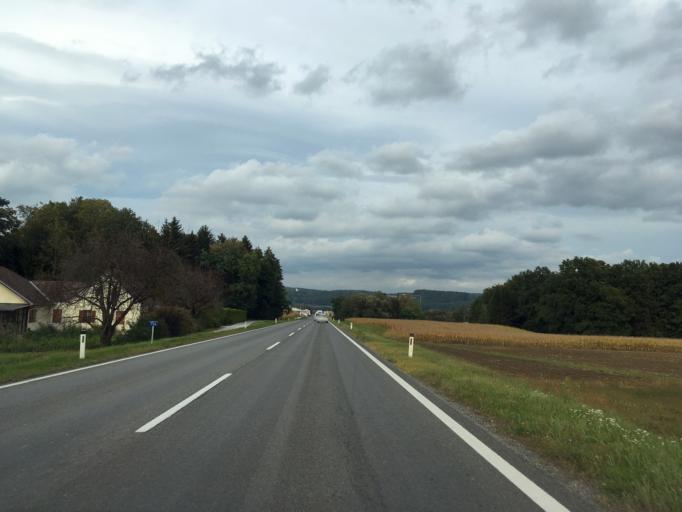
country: AT
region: Styria
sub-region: Politischer Bezirk Hartberg-Fuerstenfeld
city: Grafendorf bei Hartberg
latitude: 47.3201
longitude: 15.9861
